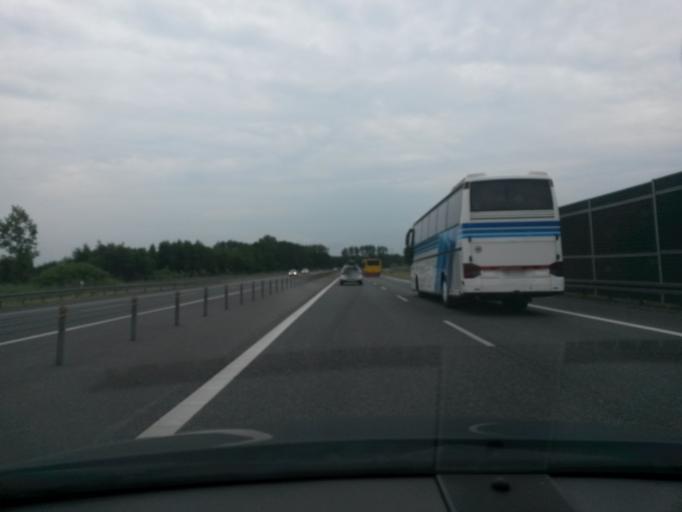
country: PL
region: Masovian Voivodeship
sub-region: Powiat zyrardowski
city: Mszczonow
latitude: 51.9624
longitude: 20.4994
